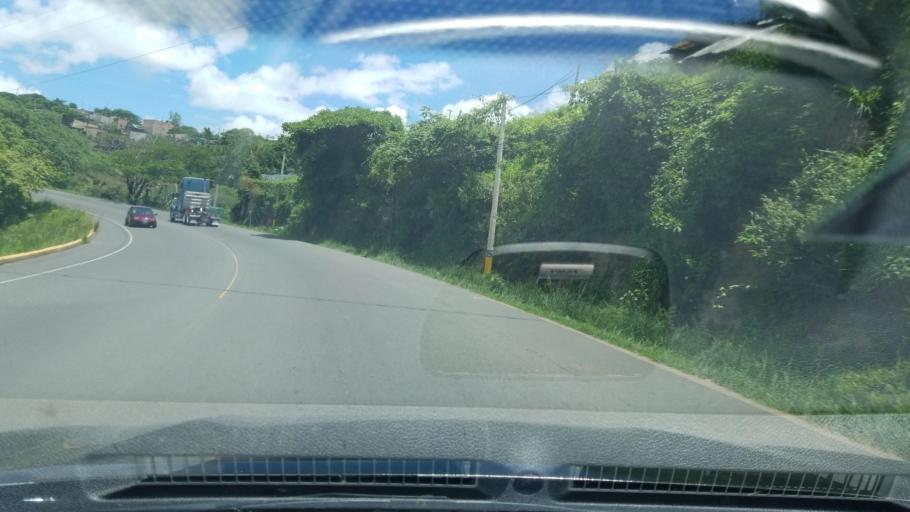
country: HN
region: Francisco Morazan
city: Rio Abajo
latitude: 14.1498
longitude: -87.2135
